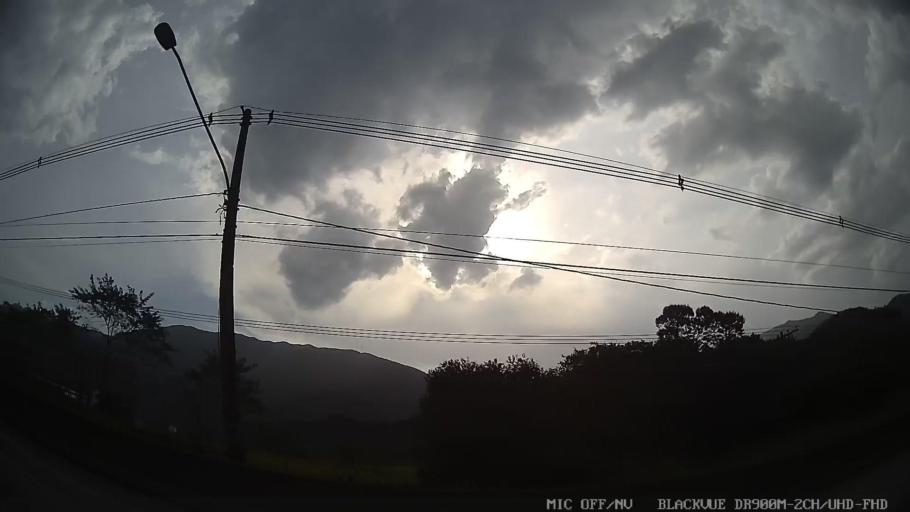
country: BR
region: Sao Paulo
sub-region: Cubatao
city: Cubatao
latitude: -23.8563
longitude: -46.4098
